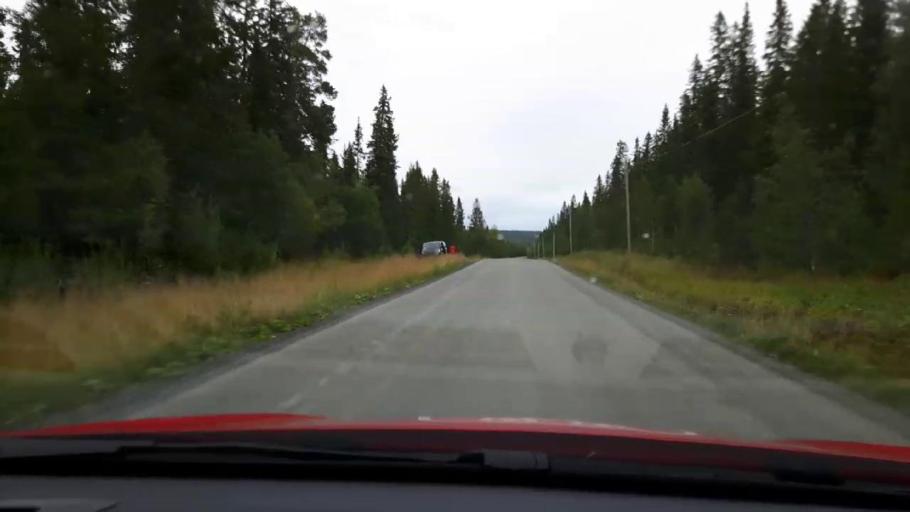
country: SE
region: Jaemtland
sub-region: Are Kommun
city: Jarpen
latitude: 63.4284
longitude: 13.3226
